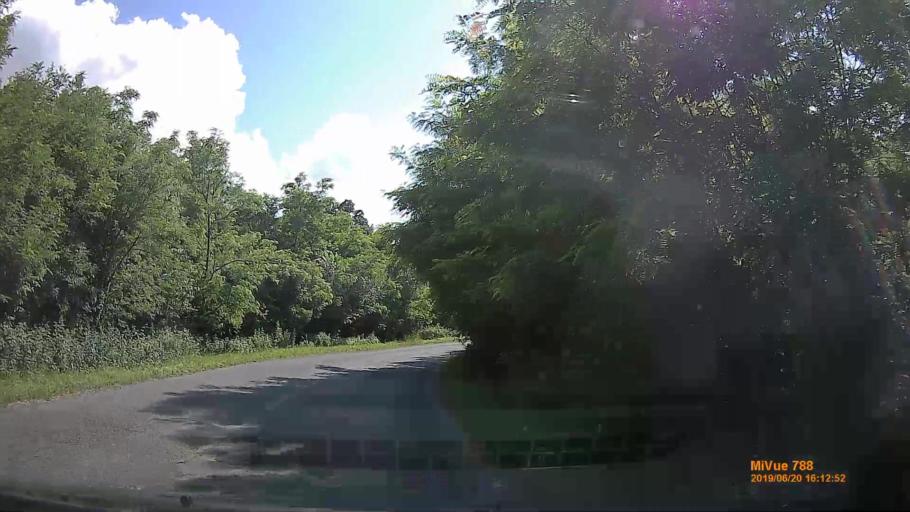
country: HU
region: Baranya
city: Pellerd
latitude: 46.0988
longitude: 18.0925
